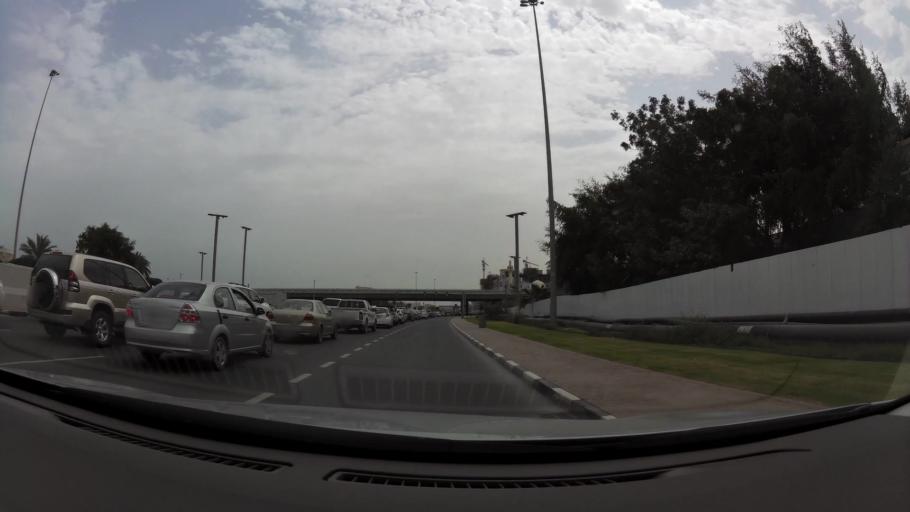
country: QA
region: Baladiyat ad Dawhah
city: Doha
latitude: 25.2848
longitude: 51.5515
